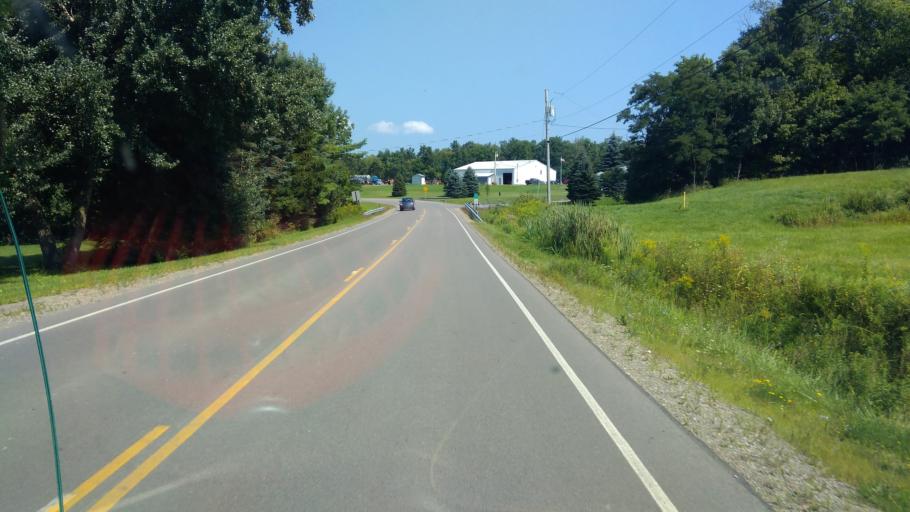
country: US
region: New York
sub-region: Allegany County
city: Belmont
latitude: 42.2595
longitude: -78.0382
